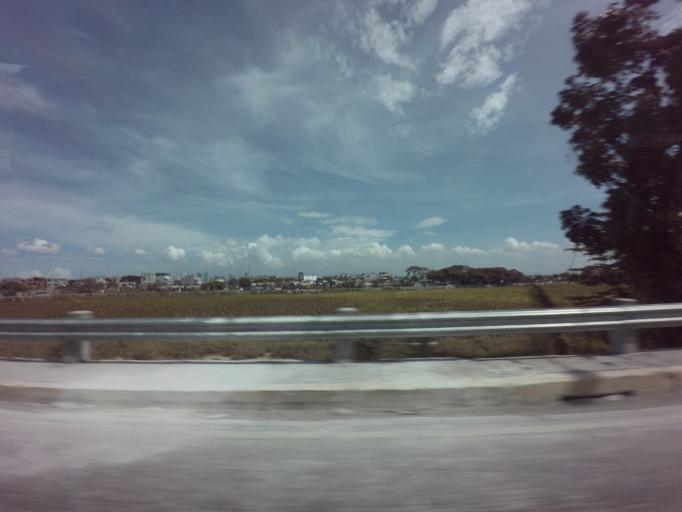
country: PH
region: Calabarzon
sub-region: Province of Rizal
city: Taguig
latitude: 14.5281
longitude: 121.0916
